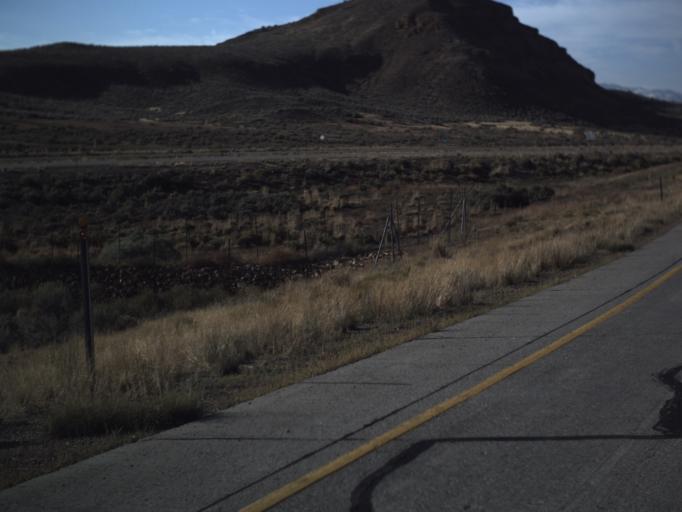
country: US
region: Utah
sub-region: Juab County
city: Nephi
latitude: 39.4356
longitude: -112.0349
